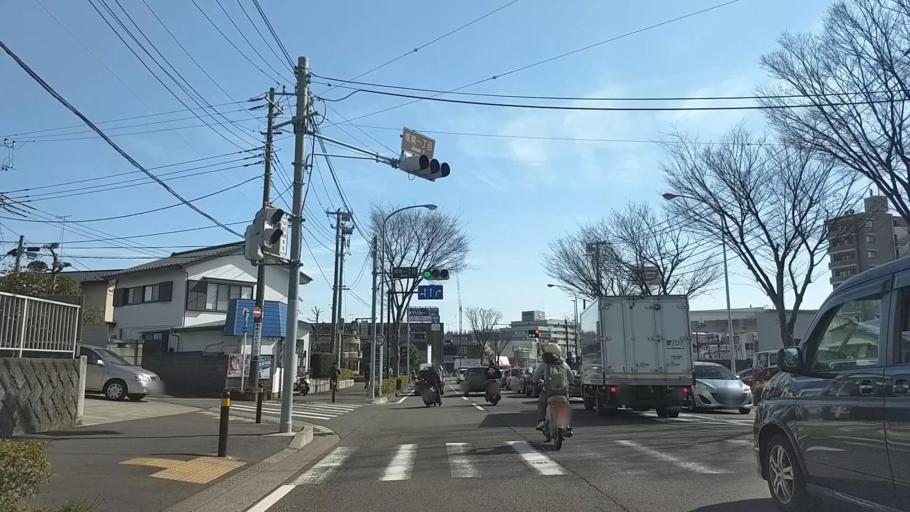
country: JP
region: Kanagawa
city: Fujisawa
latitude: 35.3465
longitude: 139.4482
